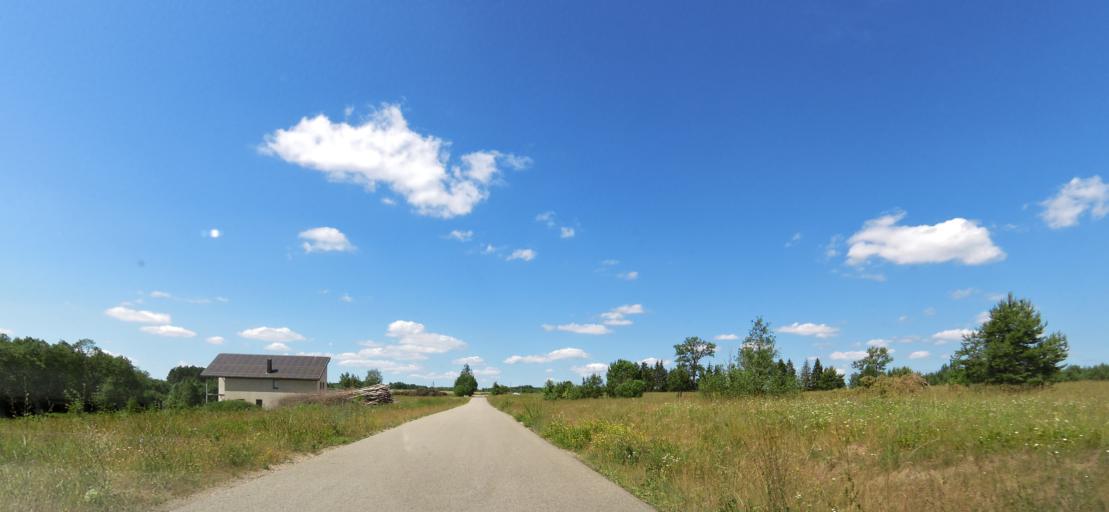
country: LT
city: Nemencine
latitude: 54.8775
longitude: 25.5333
